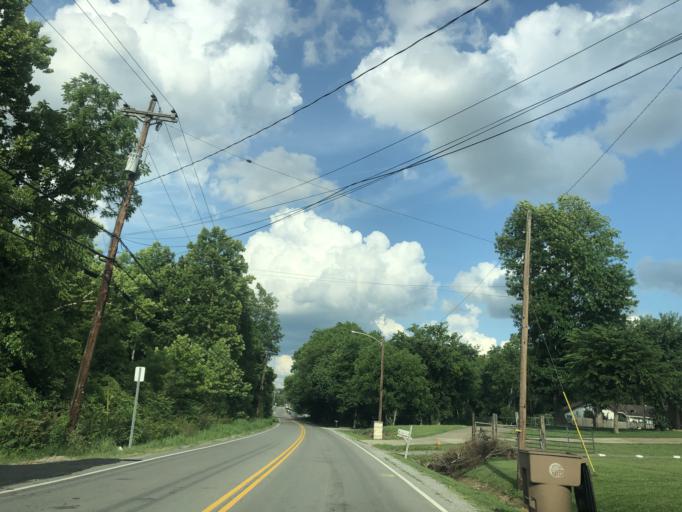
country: US
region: Tennessee
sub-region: Davidson County
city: Nashville
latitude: 36.2315
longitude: -86.7981
